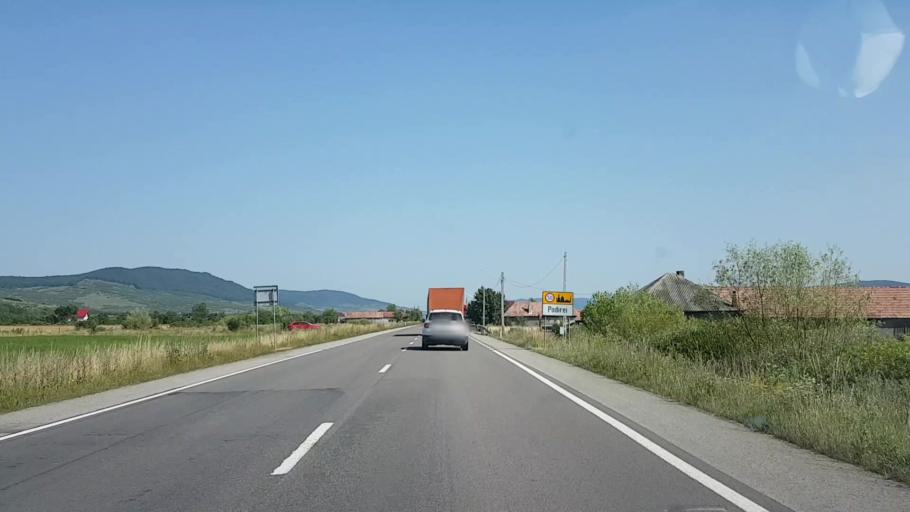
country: RO
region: Bistrita-Nasaud
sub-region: Comuna Sieu-Odorhei
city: Sieu-Odorhei
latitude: 47.1194
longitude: 24.3283
